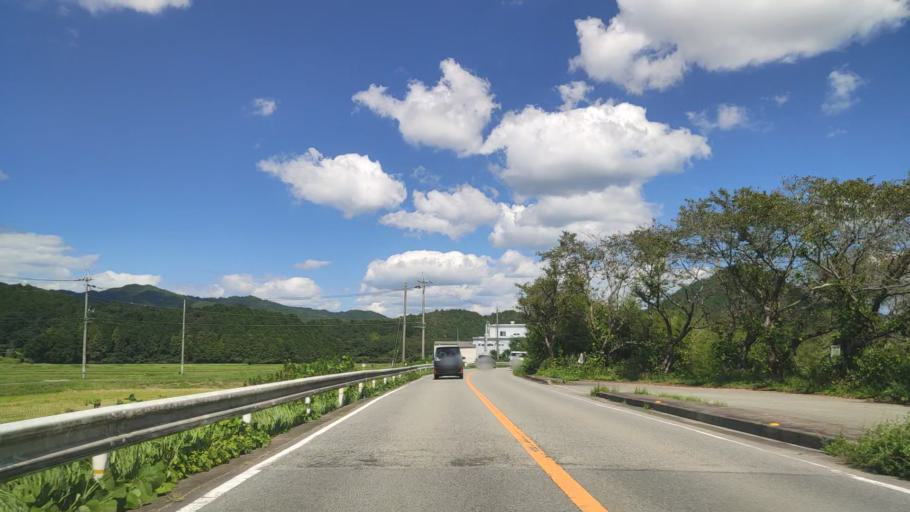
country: JP
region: Kyoto
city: Fukuchiyama
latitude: 35.1813
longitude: 135.1225
